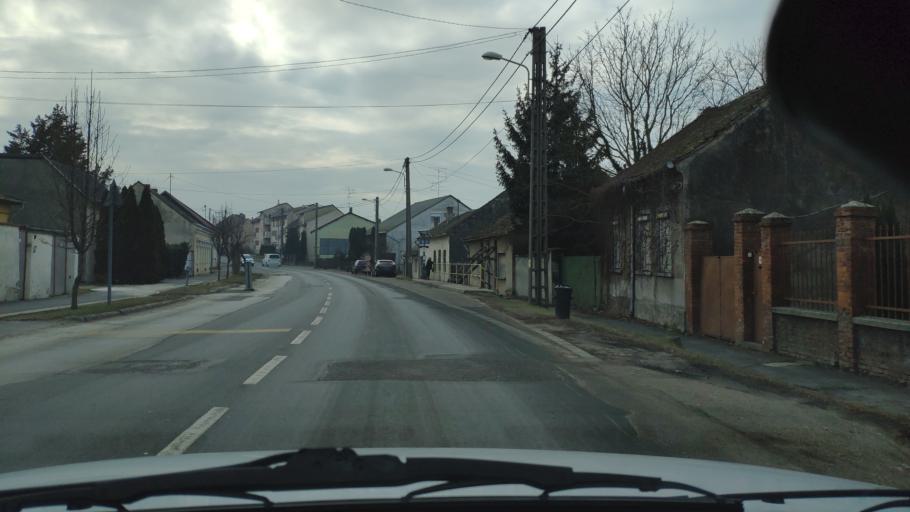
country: HU
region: Zala
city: Nagykanizsa
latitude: 46.4629
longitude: 16.9858
